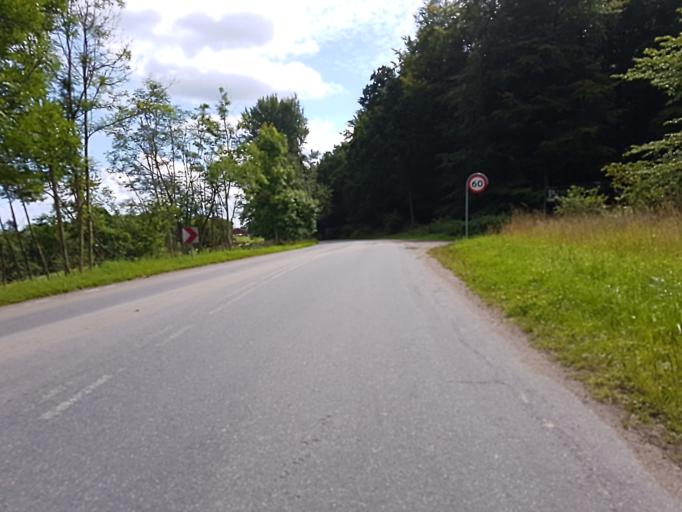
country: DK
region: Capital Region
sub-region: Allerod Kommune
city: Lynge
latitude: 55.8142
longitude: 12.3139
